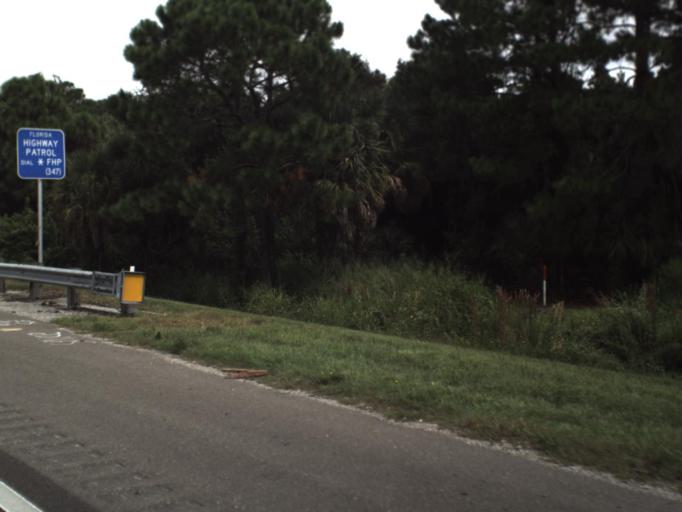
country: US
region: Florida
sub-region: Sarasota County
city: The Meadows
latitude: 27.3963
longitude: -82.4507
